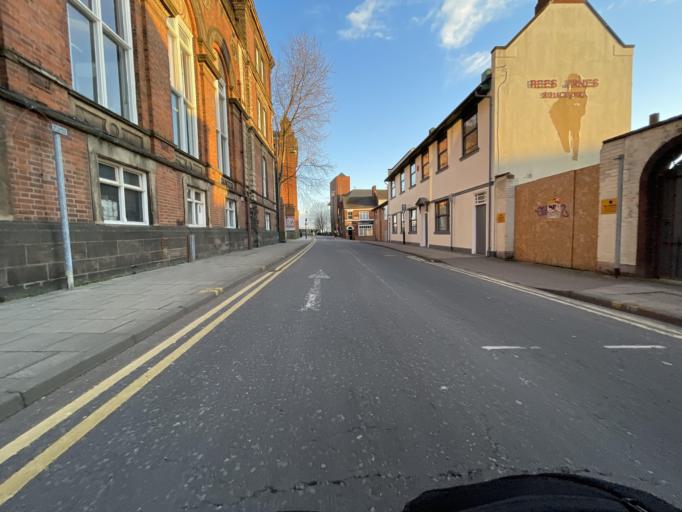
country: GB
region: England
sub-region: Stoke-on-Trent
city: Stoke-on-Trent
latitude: 53.0235
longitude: -2.1758
